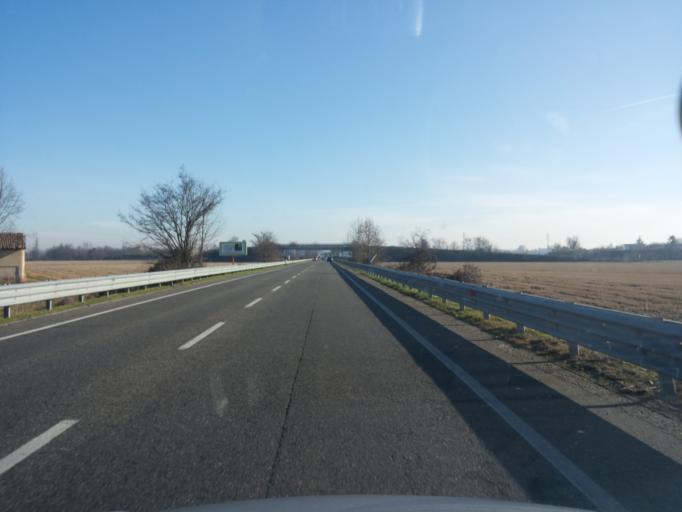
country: IT
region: Piedmont
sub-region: Provincia di Vercelli
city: Vercelli
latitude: 45.3413
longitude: 8.4153
